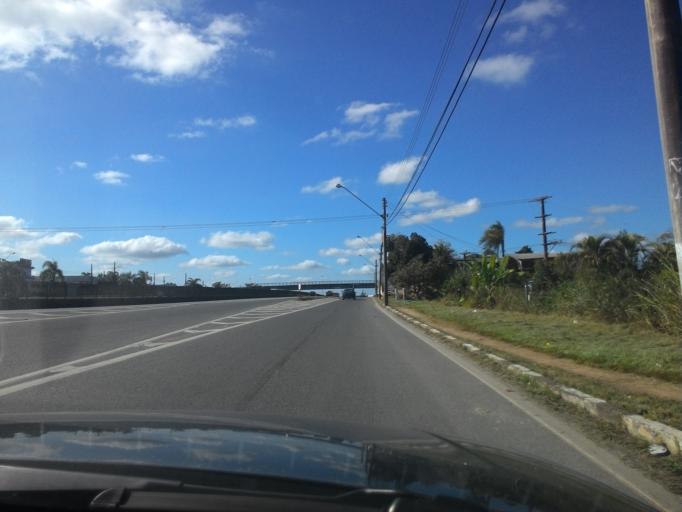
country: BR
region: Sao Paulo
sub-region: Registro
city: Registro
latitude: -24.4962
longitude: -47.8401
